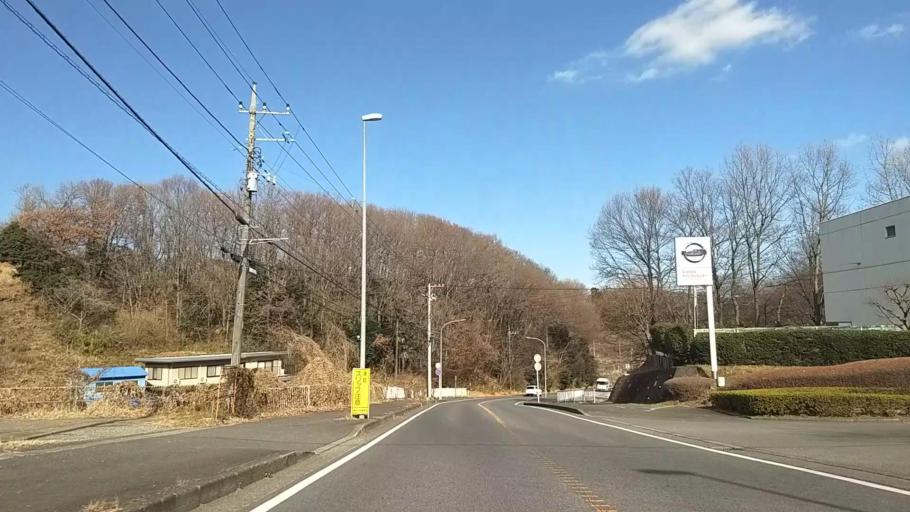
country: JP
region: Kanagawa
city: Isehara
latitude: 35.4281
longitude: 139.3051
